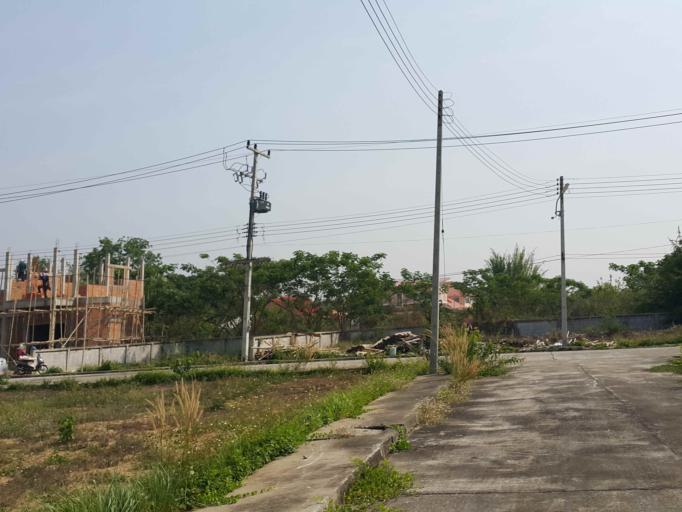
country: TH
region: Chiang Mai
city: San Kamphaeng
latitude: 18.7602
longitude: 99.0821
